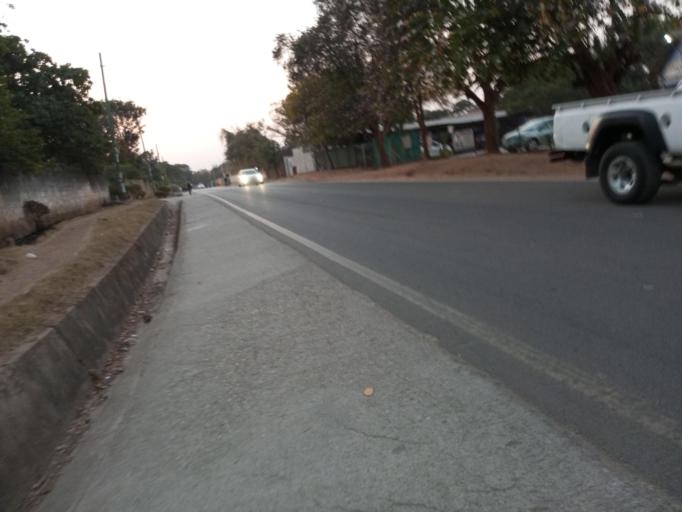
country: ZM
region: Lusaka
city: Lusaka
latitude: -15.4014
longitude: 28.2969
